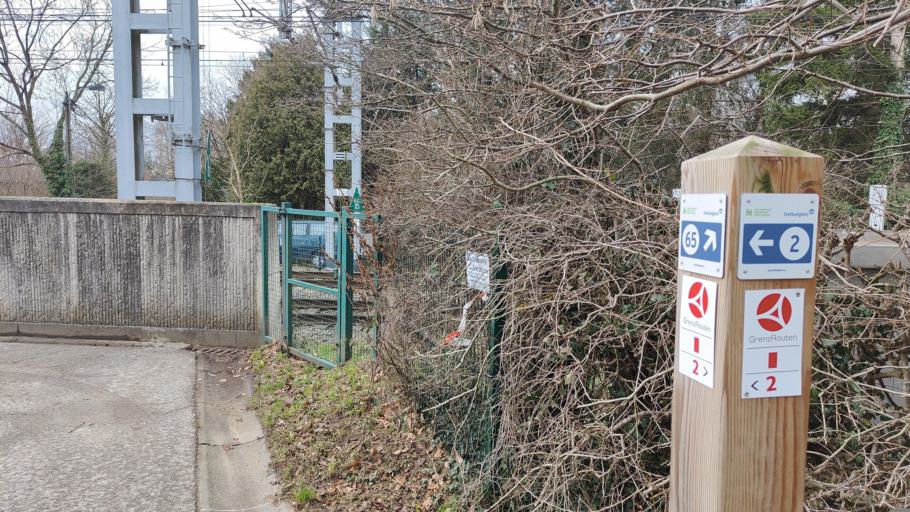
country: BE
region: Wallonia
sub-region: Province de Liege
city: La Calamine
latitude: 50.7186
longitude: 6.0415
